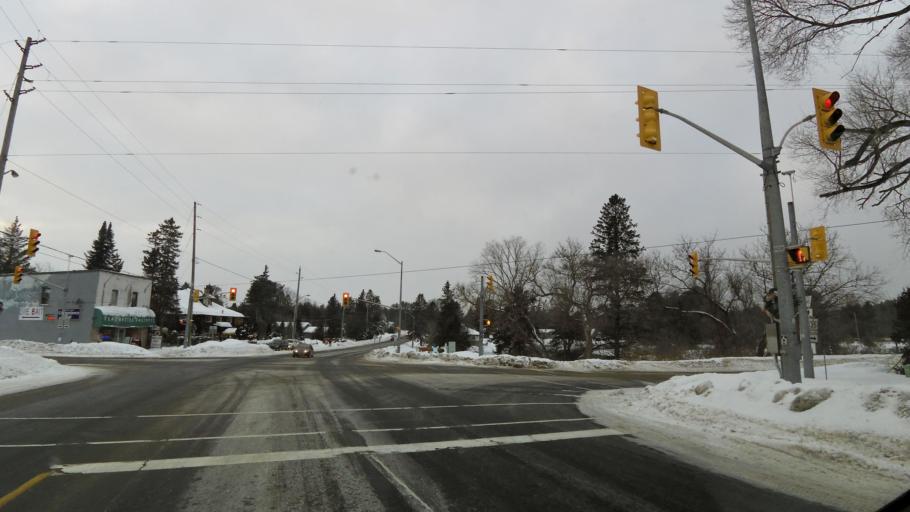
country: CA
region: Ontario
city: Omemee
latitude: 44.7274
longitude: -78.8113
